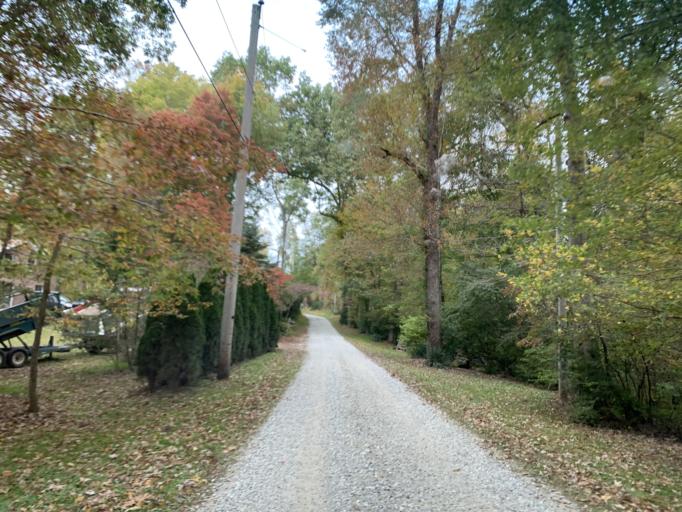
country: US
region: Pennsylvania
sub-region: York County
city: Susquehanna Trails
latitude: 39.8007
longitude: -76.4314
